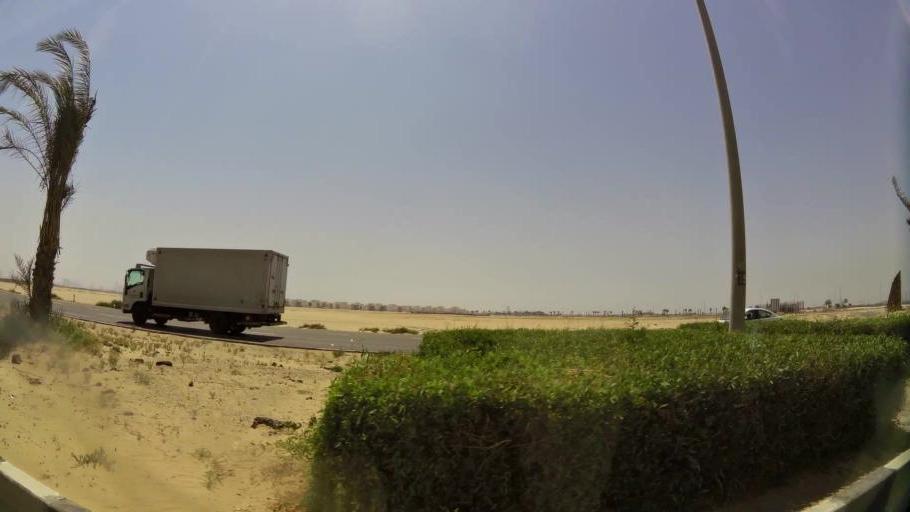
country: AE
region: Ajman
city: Ajman
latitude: 25.4327
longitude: 55.5037
